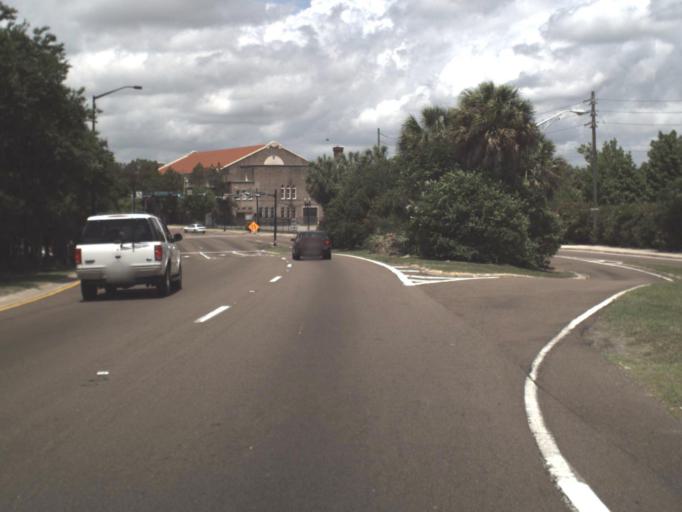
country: US
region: Florida
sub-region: Duval County
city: Jacksonville
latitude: 30.3311
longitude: -81.6498
